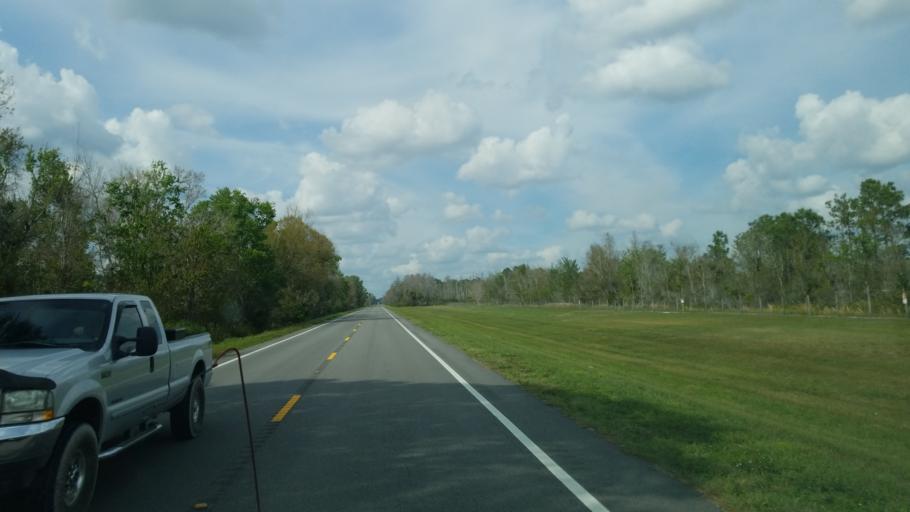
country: US
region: Florida
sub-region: Indian River County
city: Fellsmere
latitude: 27.7716
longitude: -80.9197
